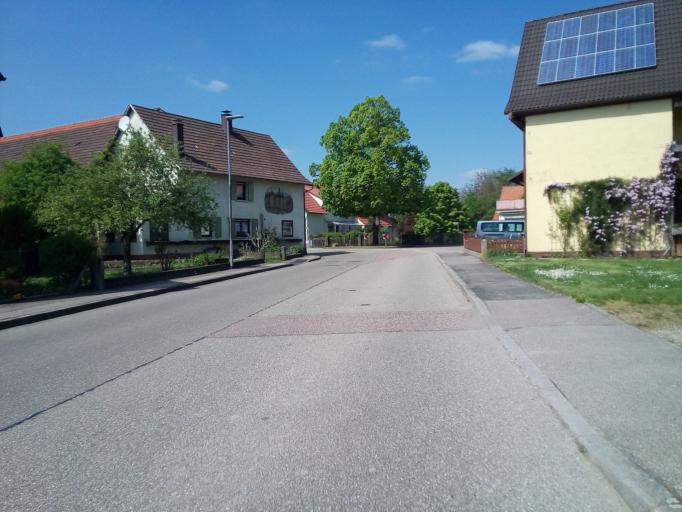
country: DE
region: Baden-Wuerttemberg
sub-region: Freiburg Region
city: Rheinau
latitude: 48.6481
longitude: 7.8950
